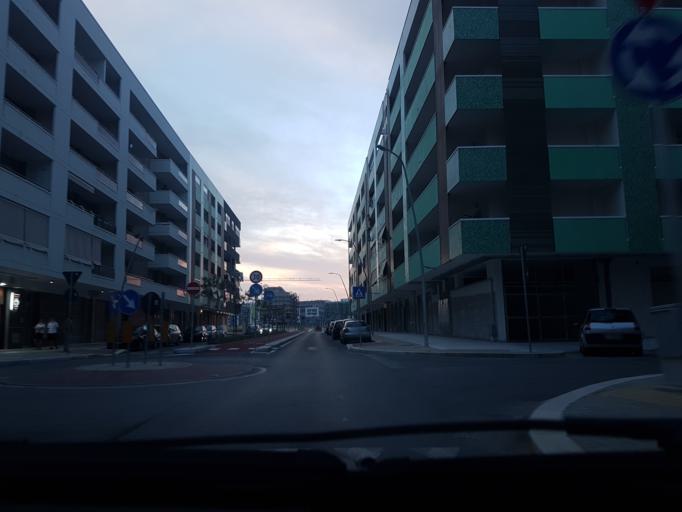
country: IT
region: Apulia
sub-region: Provincia di Barletta - Andria - Trani
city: Barletta
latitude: 41.3044
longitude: 16.2727
